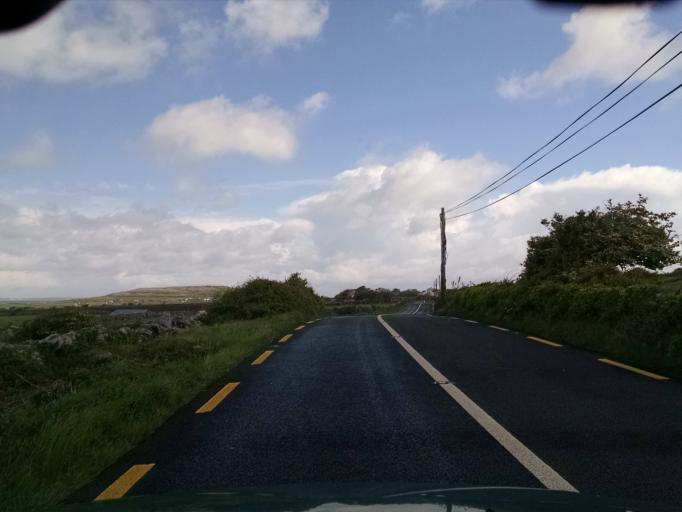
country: IE
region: Connaught
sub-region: County Galway
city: Bearna
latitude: 53.1295
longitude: -9.1207
